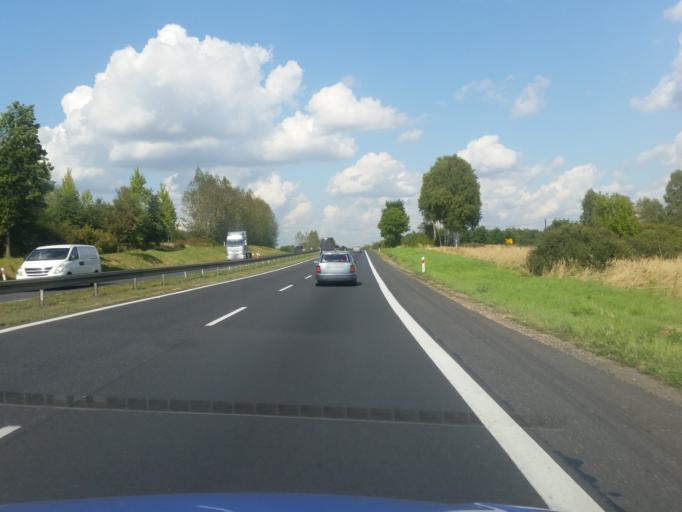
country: PL
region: Silesian Voivodeship
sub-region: Powiat czestochowski
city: Kamienica Polska
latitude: 50.6348
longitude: 19.1360
